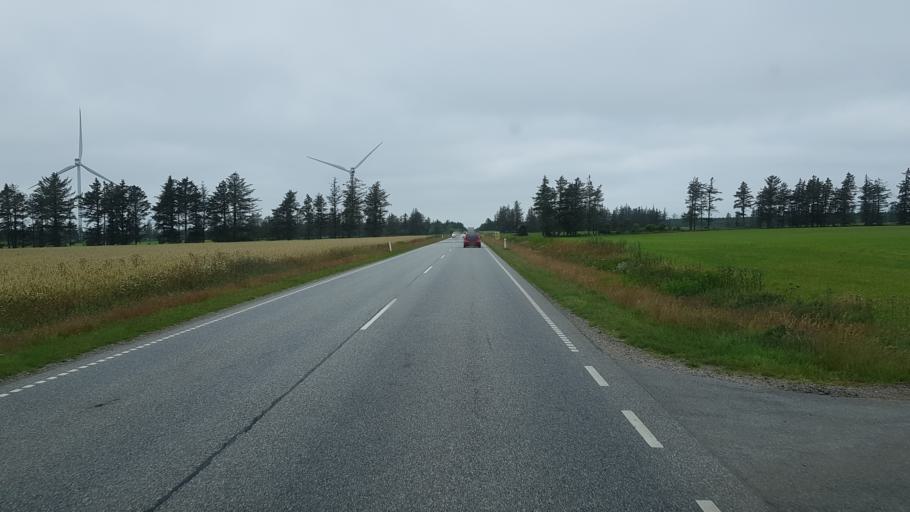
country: DK
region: Central Jutland
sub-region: Lemvig Kommune
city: Lemvig
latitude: 56.4445
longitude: 8.3595
